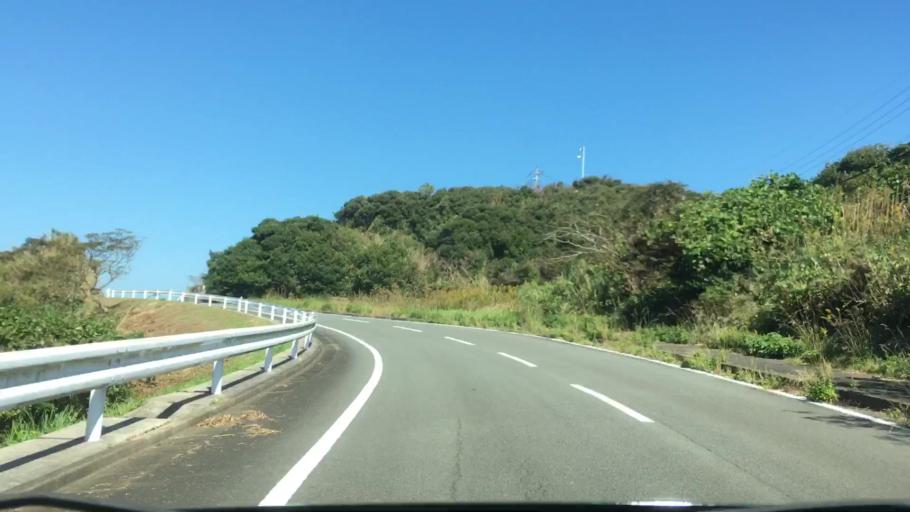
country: JP
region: Nagasaki
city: Sasebo
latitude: 33.0098
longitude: 129.5675
